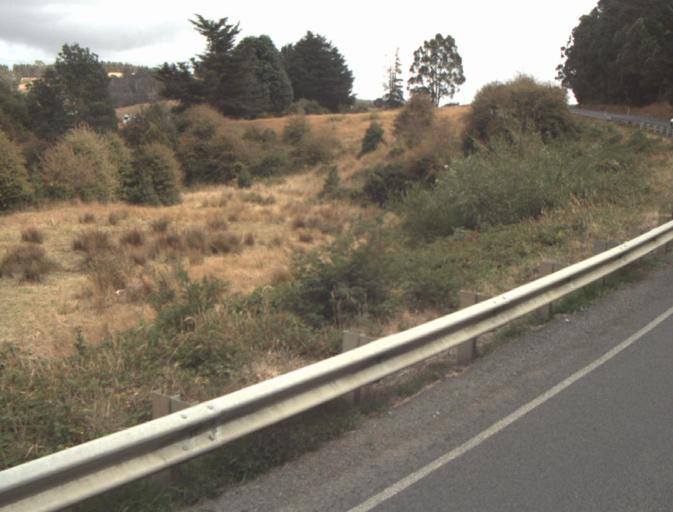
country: AU
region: Tasmania
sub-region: Launceston
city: Mayfield
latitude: -41.2280
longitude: 147.2090
